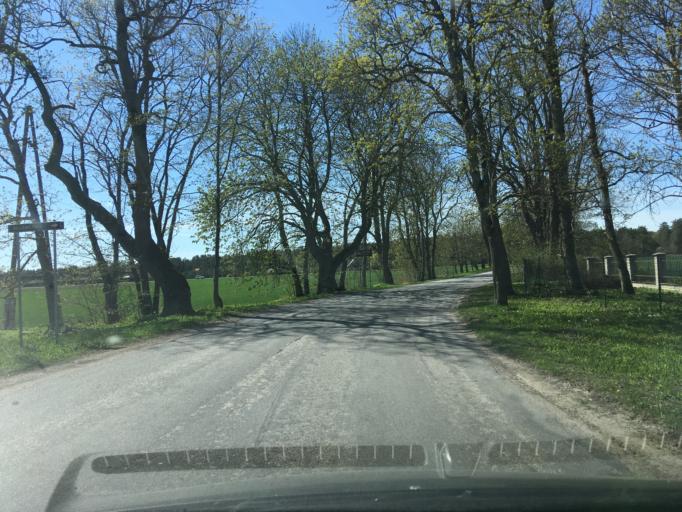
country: EE
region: Harju
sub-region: Raasiku vald
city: Arukula
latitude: 59.3571
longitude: 25.0815
